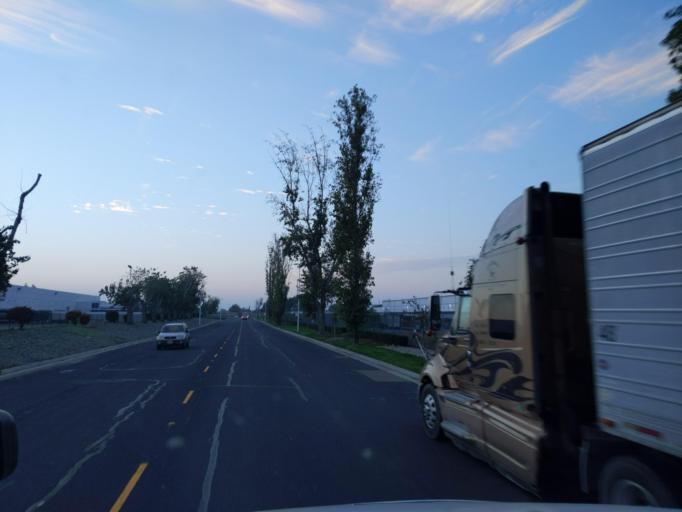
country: US
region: California
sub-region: San Joaquin County
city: Lathrop
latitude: 37.7982
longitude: -121.2951
